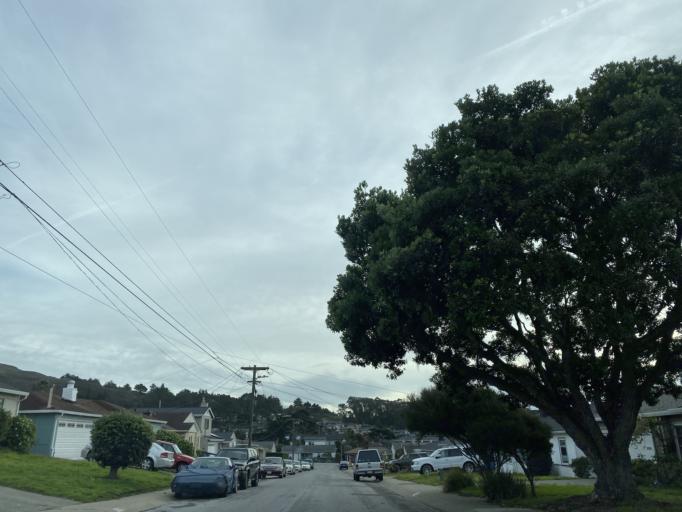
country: US
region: California
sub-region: San Mateo County
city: Pacifica
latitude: 37.6486
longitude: -122.4869
